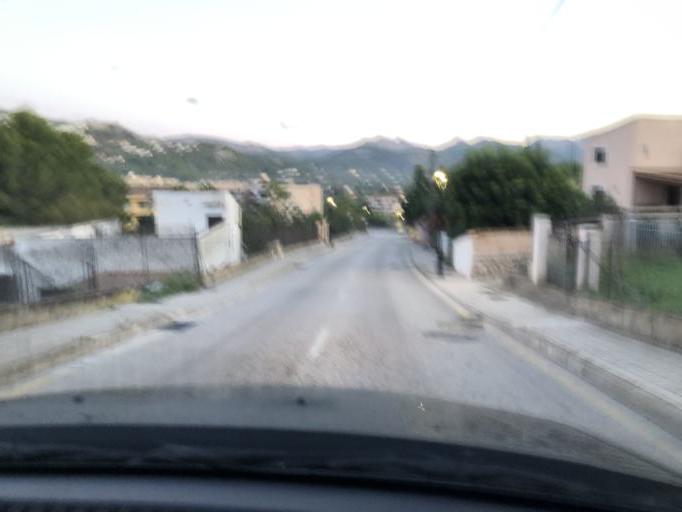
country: ES
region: Balearic Islands
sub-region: Illes Balears
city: Camp de Mar
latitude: 39.5434
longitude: 2.3926
